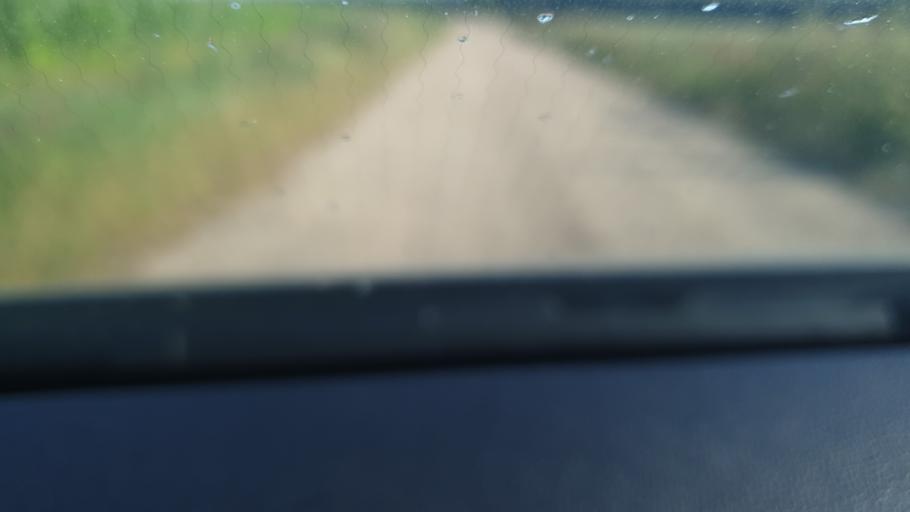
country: DE
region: Mecklenburg-Vorpommern
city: Torgelow
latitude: 53.6475
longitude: 13.9510
